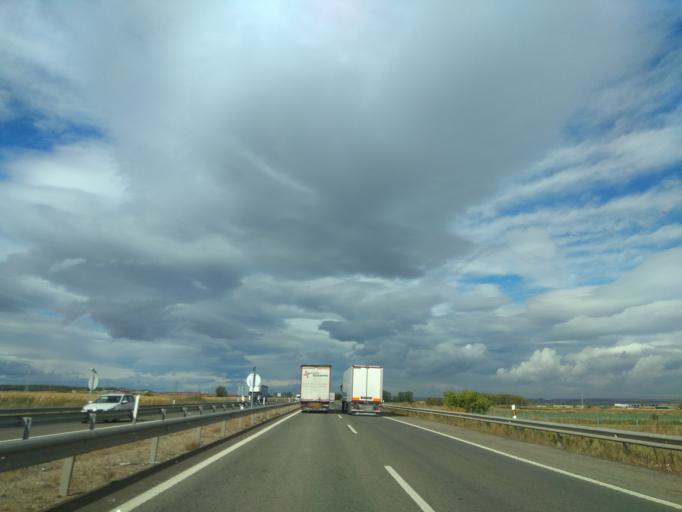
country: ES
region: Navarre
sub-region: Provincia de Navarra
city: Ribaforada
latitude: 41.9755
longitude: -1.5145
